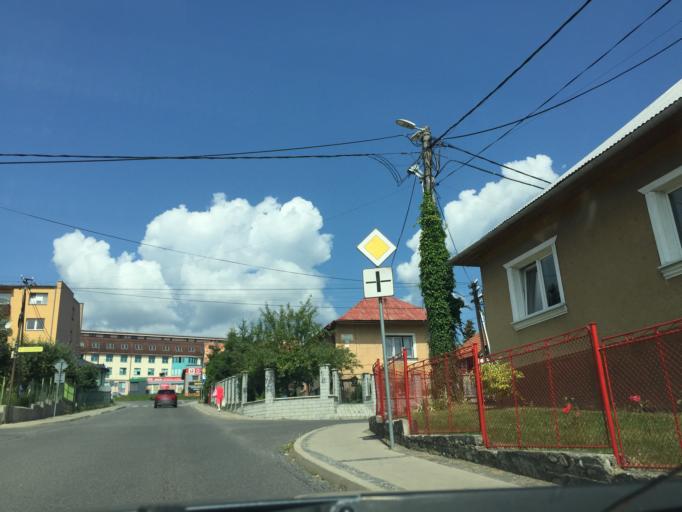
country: SK
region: Zilinsky
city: Namestovo
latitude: 49.4043
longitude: 19.4763
